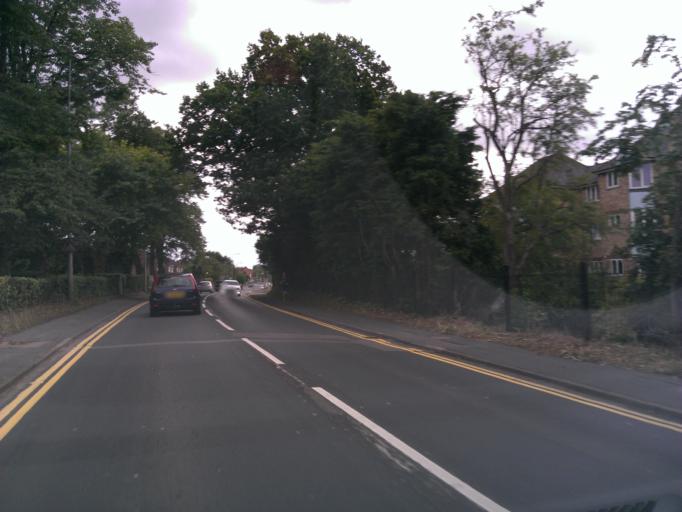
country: GB
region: England
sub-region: Essex
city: Colchester
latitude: 51.9121
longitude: 0.9283
